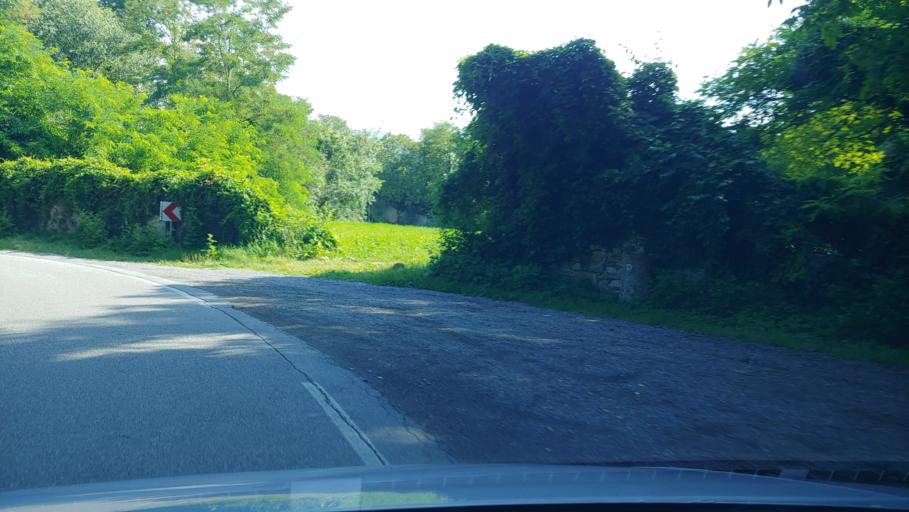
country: SI
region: Komen
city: Komen
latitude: 45.8501
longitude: 13.7920
